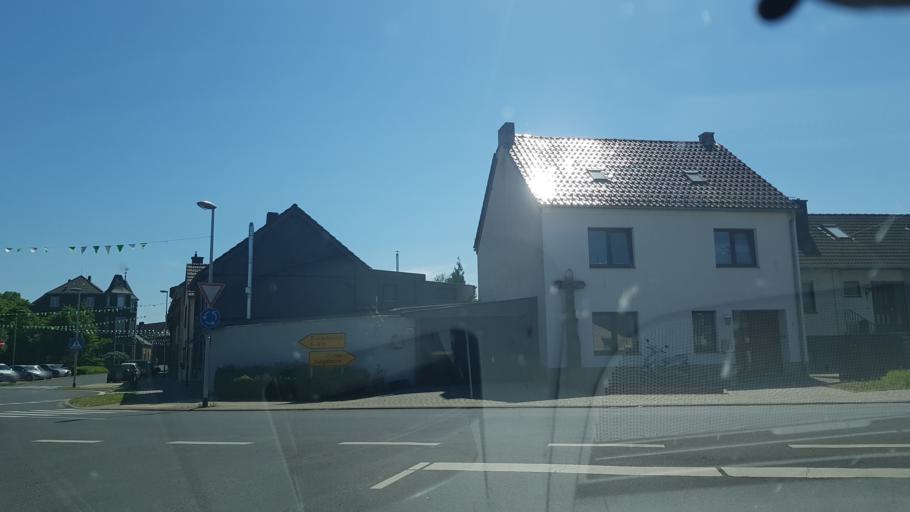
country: DE
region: North Rhine-Westphalia
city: Tuernich
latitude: 50.8020
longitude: 6.7251
